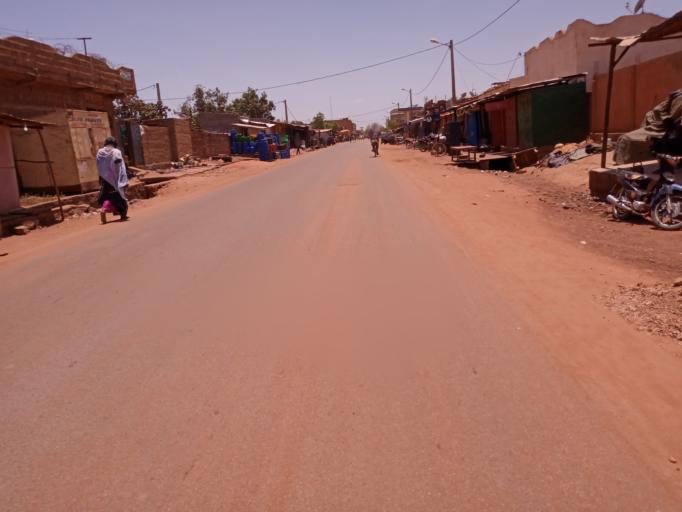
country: ML
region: Bamako
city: Bamako
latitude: 12.5767
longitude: -7.9707
